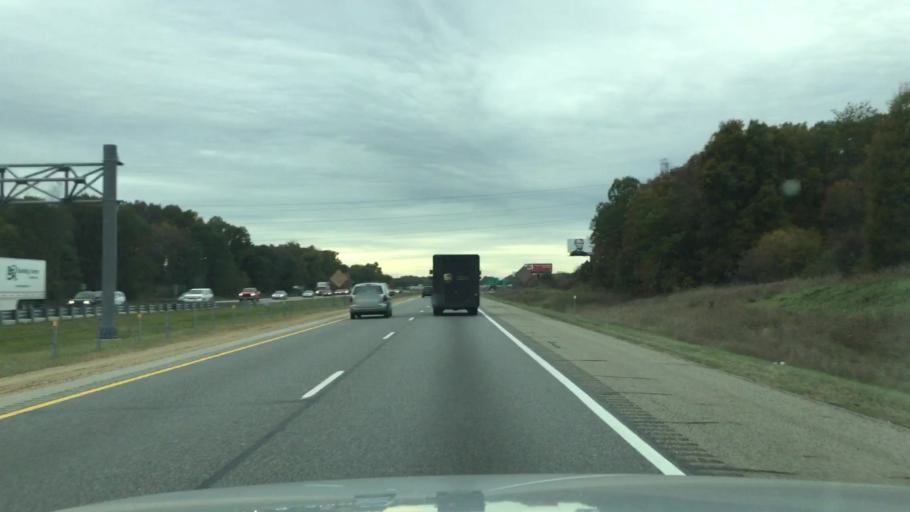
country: US
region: Michigan
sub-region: Kalamazoo County
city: Westwood
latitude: 42.2378
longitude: -85.6643
